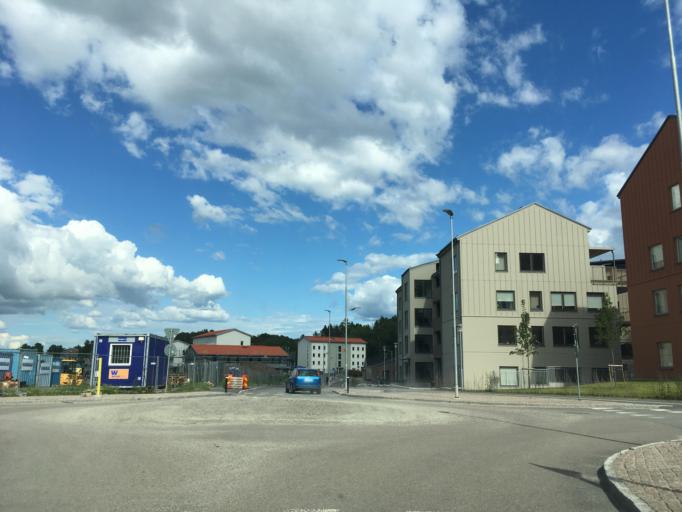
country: SE
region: Vaestra Goetaland
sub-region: Kungalvs Kommun
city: Kungalv
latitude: 57.8593
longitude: 11.9002
